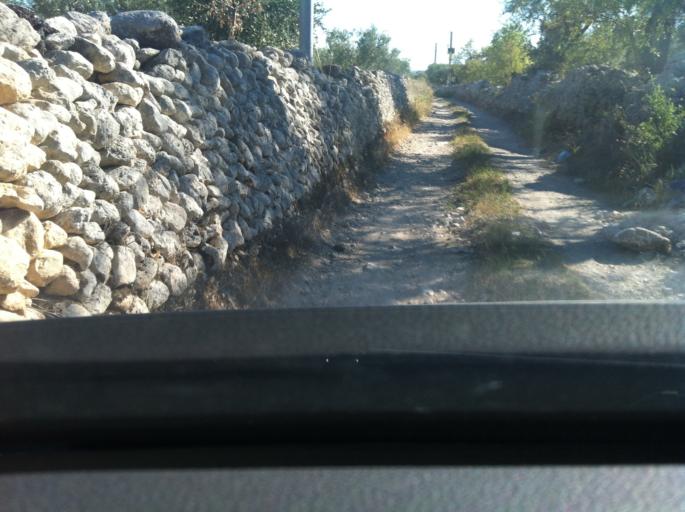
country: IT
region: Apulia
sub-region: Provincia di Foggia
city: Monte Sant'Angelo
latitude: 41.6516
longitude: 15.9618
